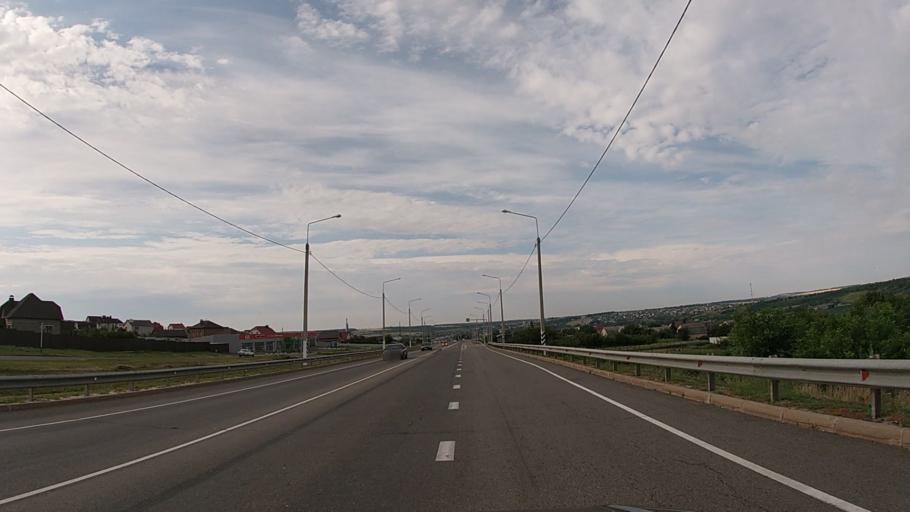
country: RU
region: Belgorod
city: Severnyy
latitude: 50.6476
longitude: 36.4682
